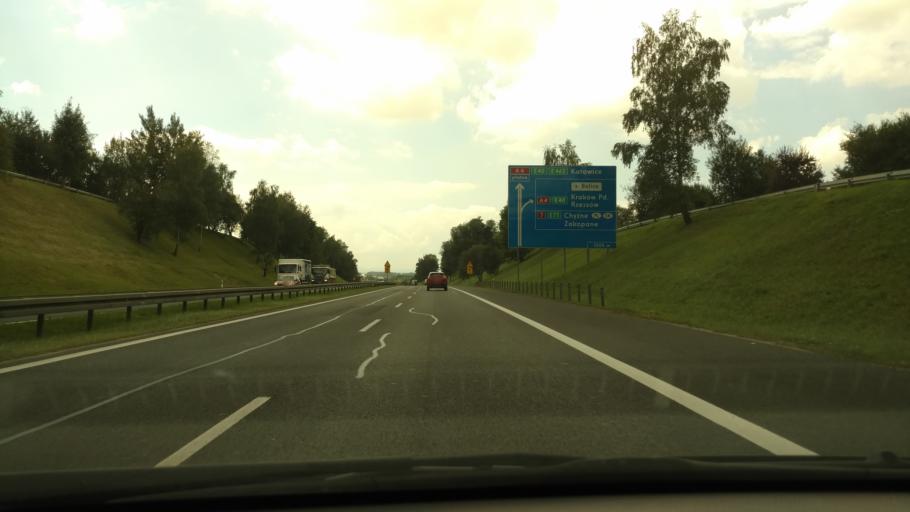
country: PL
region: Lesser Poland Voivodeship
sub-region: Powiat krakowski
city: Rzaska
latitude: 50.0975
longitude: 19.8232
